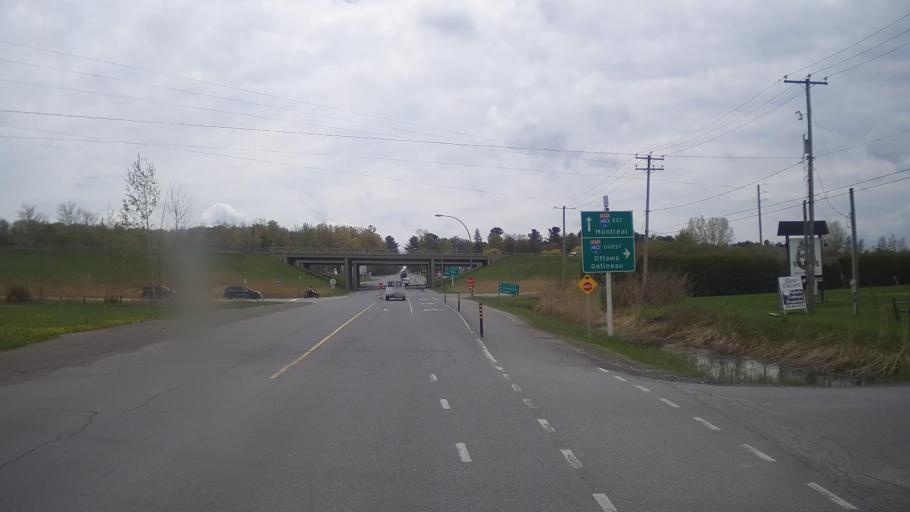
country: CA
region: Quebec
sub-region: Monteregie
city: Hudson
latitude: 45.4368
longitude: -74.1730
